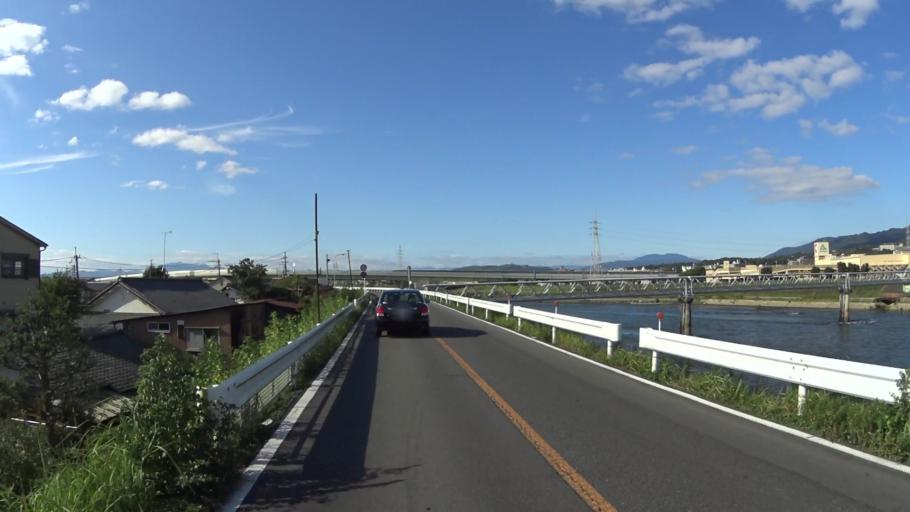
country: JP
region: Kyoto
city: Uji
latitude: 34.8964
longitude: 135.8004
